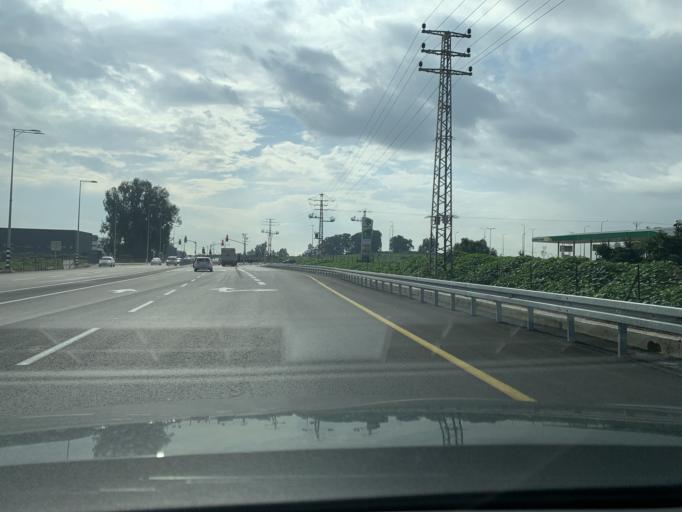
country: PS
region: West Bank
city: Qalqilyah
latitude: 32.1942
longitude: 34.9538
